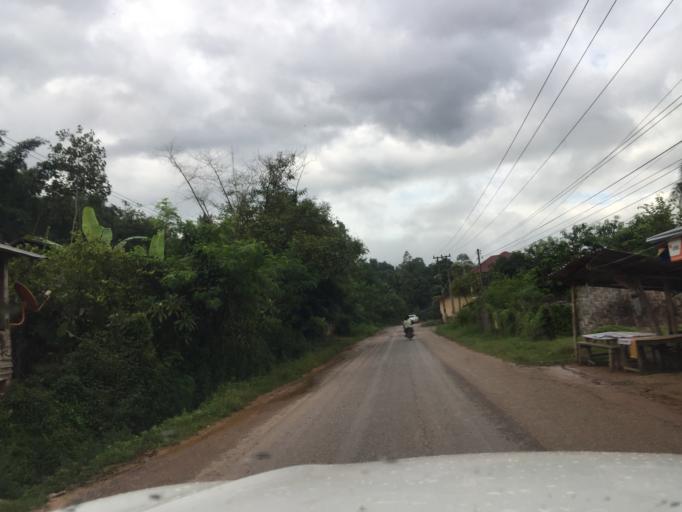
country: LA
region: Oudomxai
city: Muang La
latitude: 20.8616
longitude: 102.1155
